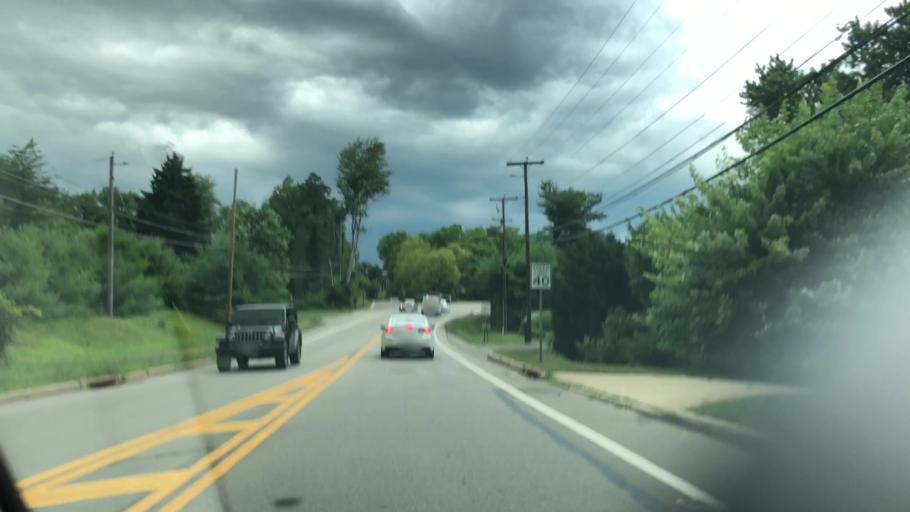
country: US
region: Ohio
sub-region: Stark County
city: Perry Heights
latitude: 40.8564
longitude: -81.4626
